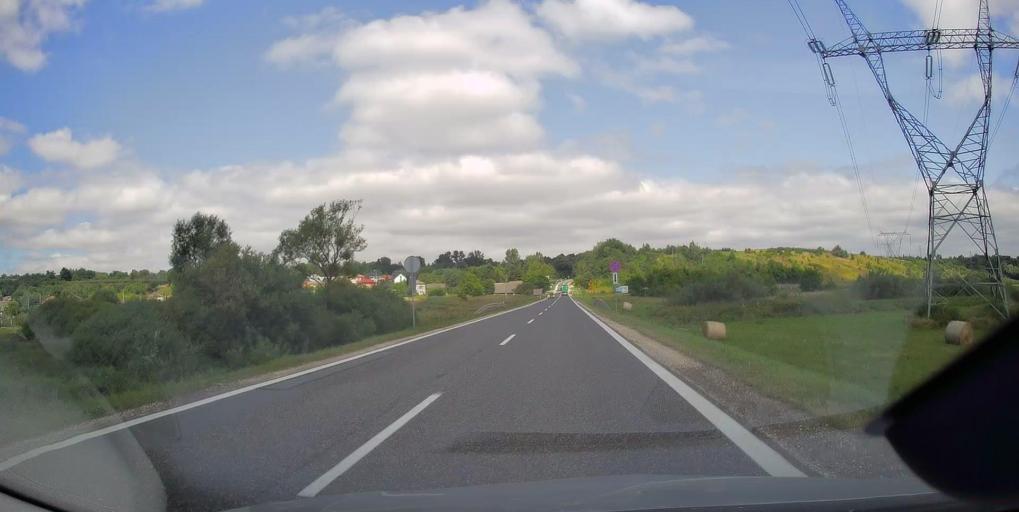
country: PL
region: Swietokrzyskie
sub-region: Powiat sandomierski
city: Klimontow
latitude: 50.6053
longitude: 21.4688
